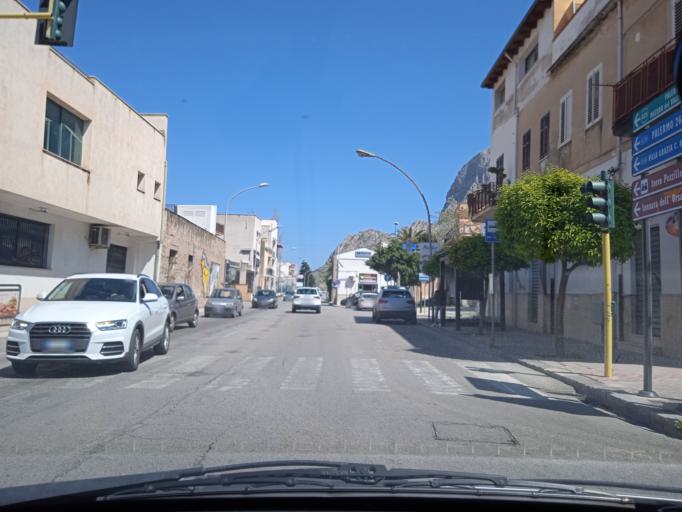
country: IT
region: Sicily
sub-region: Palermo
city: Cinisi
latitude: 38.1616
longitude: 13.1023
